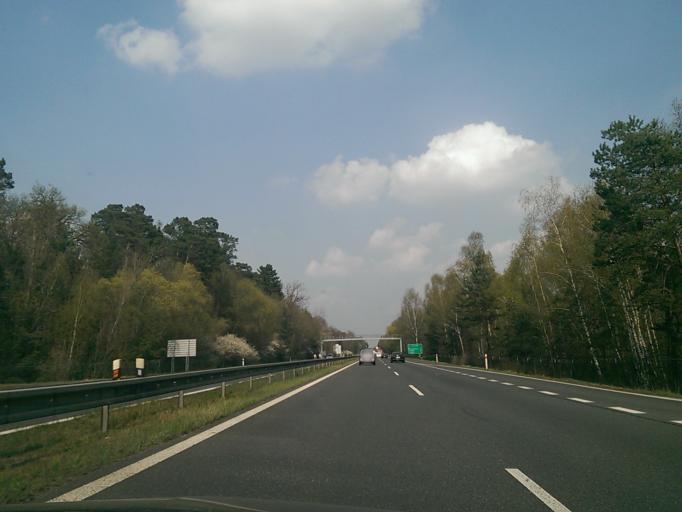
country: CZ
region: Central Bohemia
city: Brandys nad Labem-Stara Boleslav
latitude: 50.2273
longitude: 14.7228
